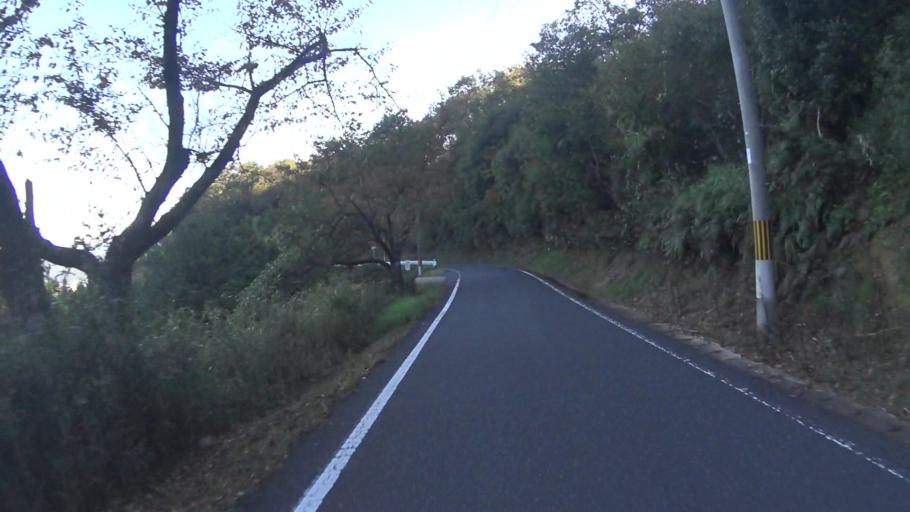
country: JP
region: Hyogo
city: Toyooka
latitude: 35.6171
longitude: 134.8722
